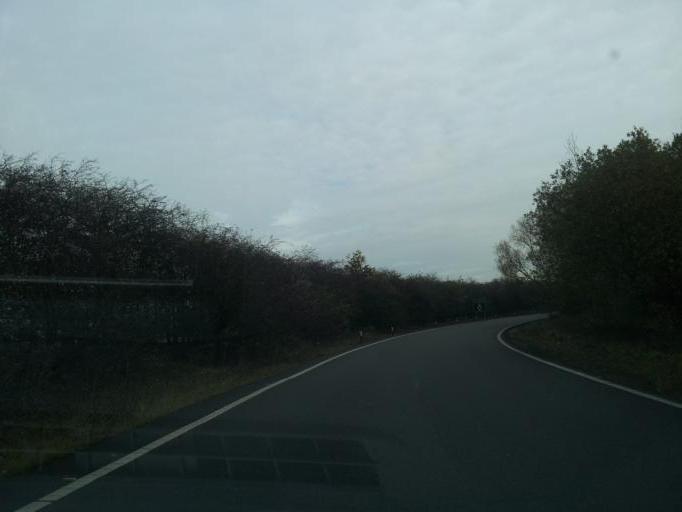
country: GB
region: England
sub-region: Cambridgeshire
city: Comberton
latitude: 52.2180
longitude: 0.0331
